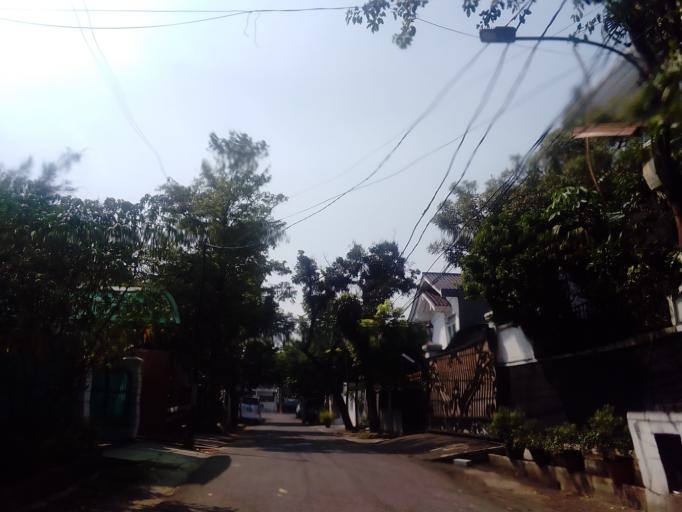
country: ID
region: Jakarta Raya
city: Jakarta
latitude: -6.2502
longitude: 106.7990
